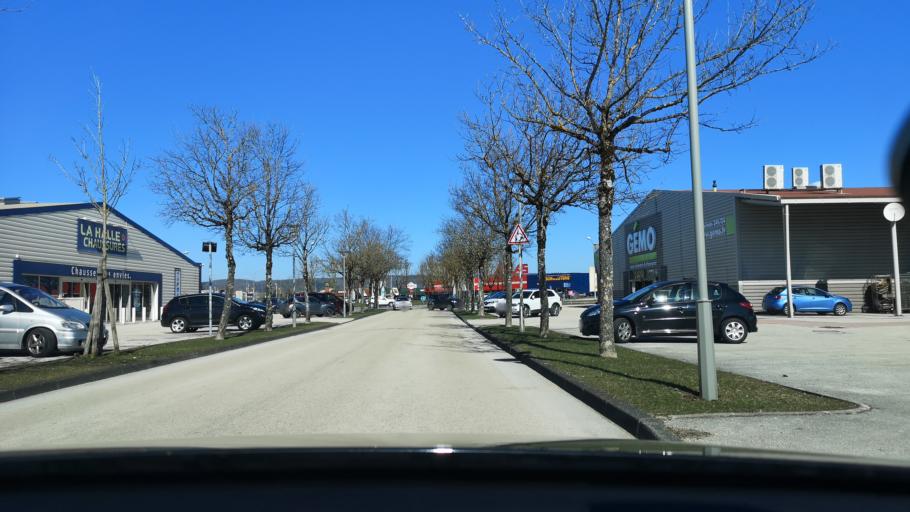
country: FR
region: Franche-Comte
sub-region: Departement du Doubs
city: Pontarlier
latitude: 46.9085
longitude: 6.3360
